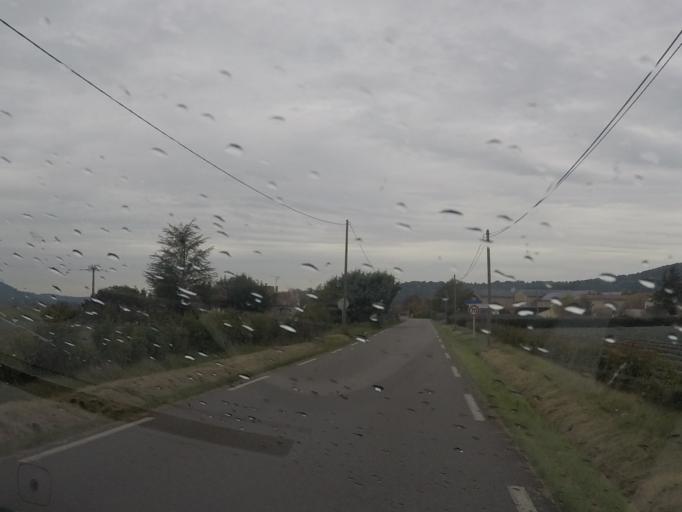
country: FR
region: Provence-Alpes-Cote d'Azur
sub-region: Departement du Vaucluse
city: Goult
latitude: 43.8519
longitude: 5.2794
